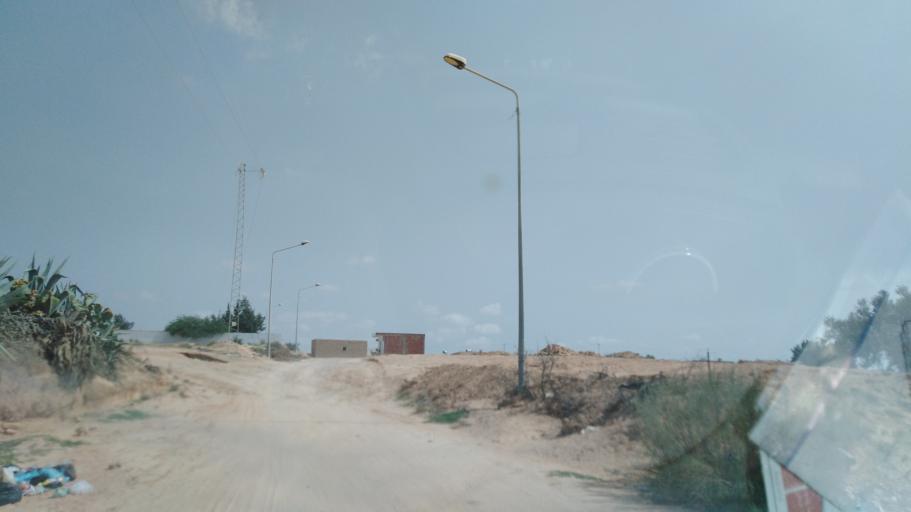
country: TN
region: Safaqis
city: Sfax
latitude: 34.6401
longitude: 10.6164
